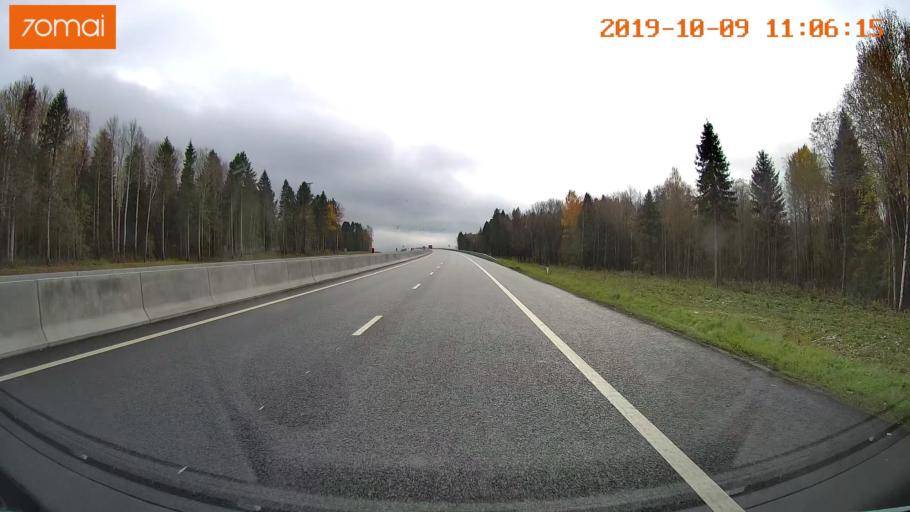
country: RU
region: Vologda
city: Vologda
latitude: 59.1890
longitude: 39.7592
